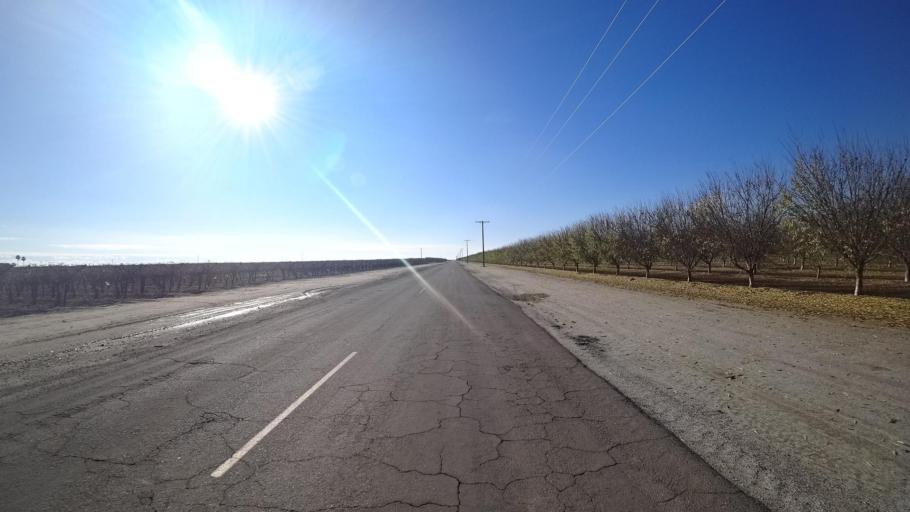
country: US
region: California
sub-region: Kern County
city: Delano
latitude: 35.7421
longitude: -119.2763
